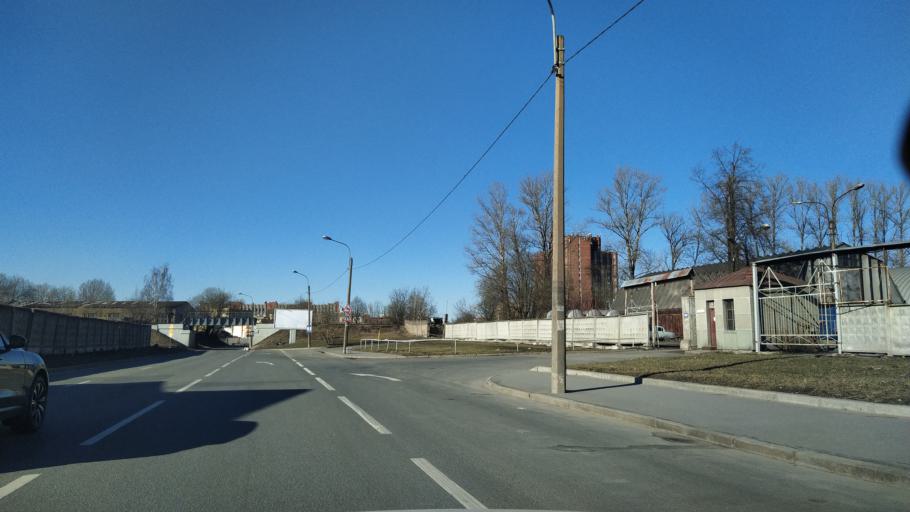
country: RU
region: St.-Petersburg
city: Centralniy
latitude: 59.9106
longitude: 30.3754
